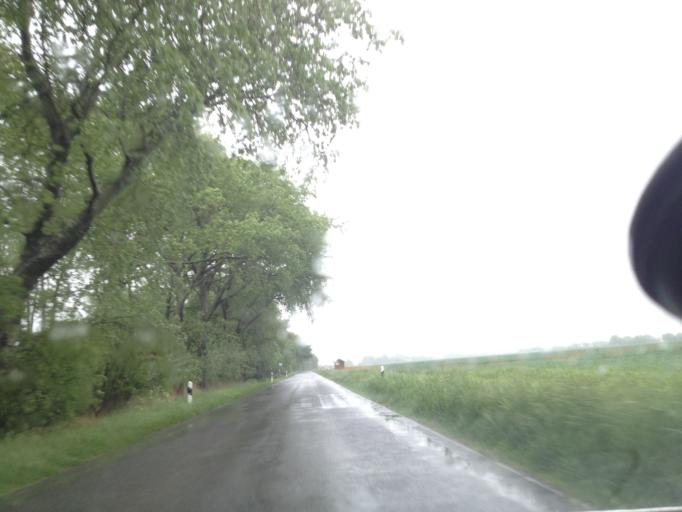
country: DE
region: Schleswig-Holstein
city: Rodenas
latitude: 54.8858
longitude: 8.7160
